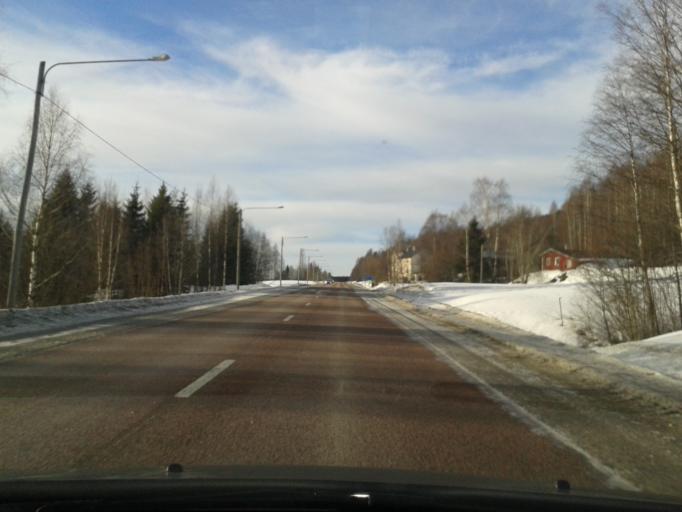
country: SE
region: Vaesternorrland
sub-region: OErnskoeldsviks Kommun
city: Bjasta
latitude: 63.3816
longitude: 18.4093
